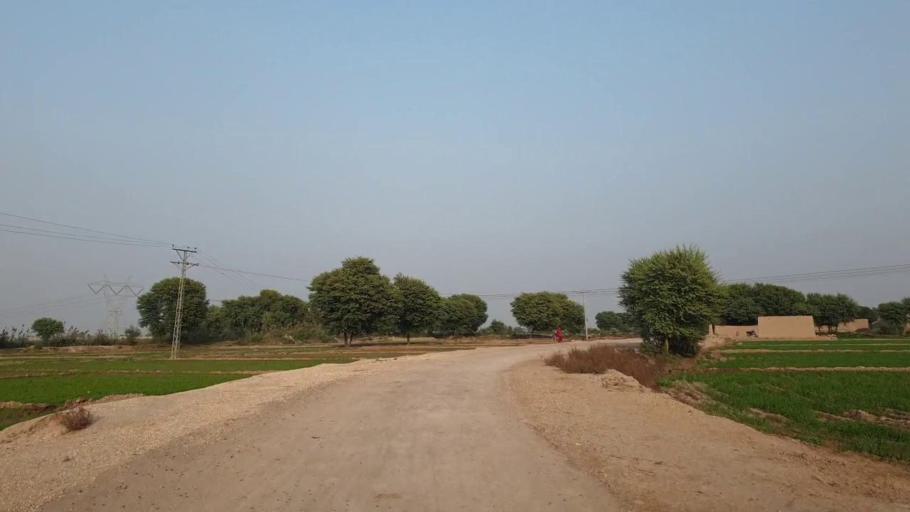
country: PK
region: Sindh
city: Bhan
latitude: 26.4973
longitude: 67.7696
